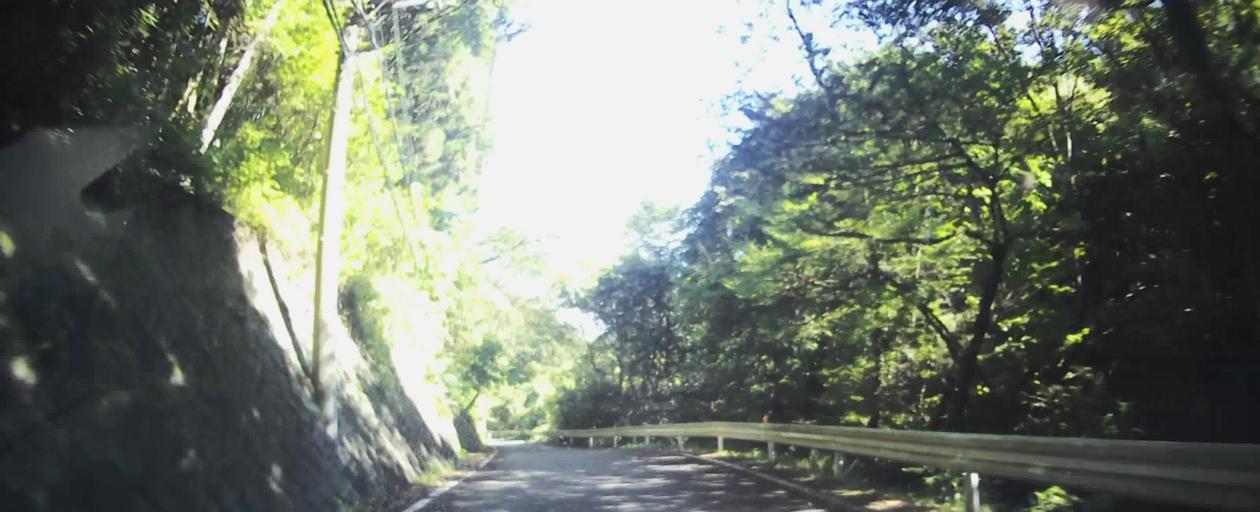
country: JP
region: Gunma
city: Nakanojomachi
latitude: 36.5770
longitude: 138.7308
